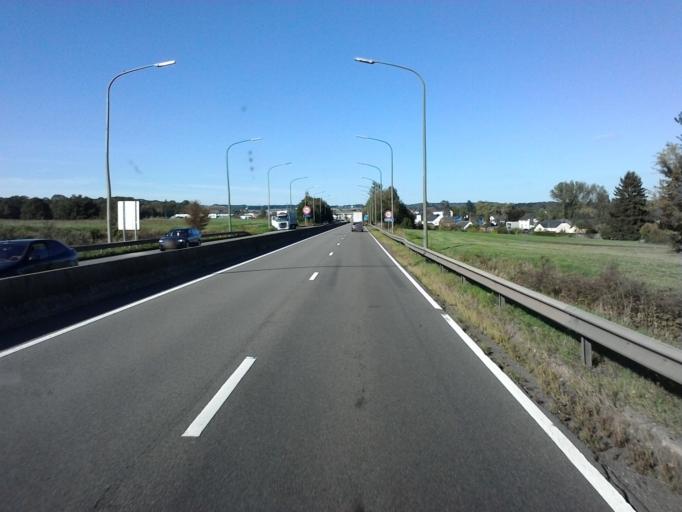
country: BE
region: Wallonia
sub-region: Province du Luxembourg
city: Messancy
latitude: 49.6030
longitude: 5.8093
